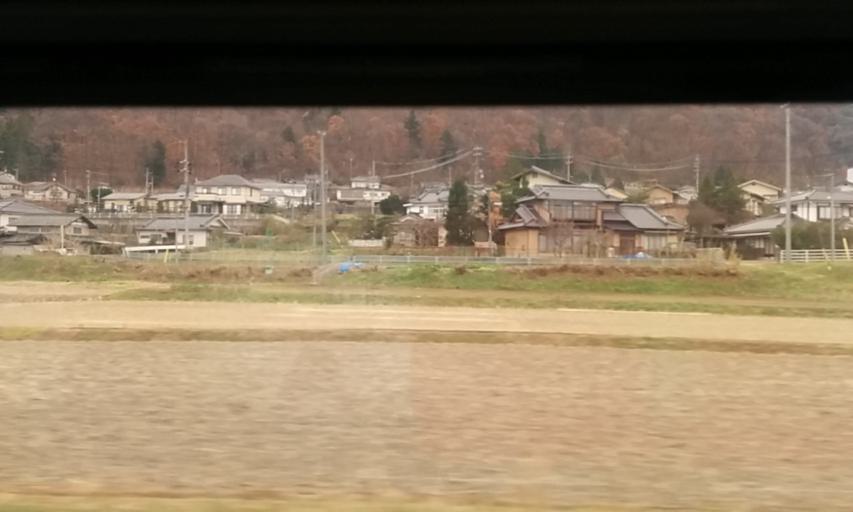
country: JP
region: Nagano
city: Hotaka
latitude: 36.3501
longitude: 137.9253
